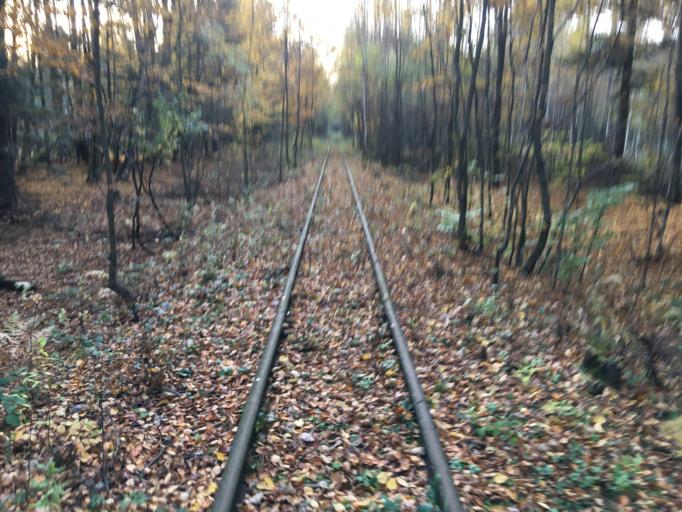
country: PL
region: Swietokrzyskie
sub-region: Powiat starachowicki
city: Brody
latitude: 51.0749
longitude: 21.1602
